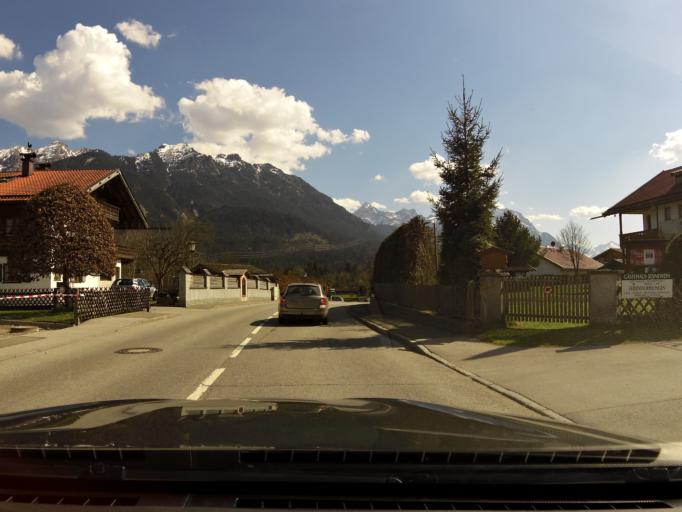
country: DE
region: Bavaria
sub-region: Upper Bavaria
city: Wallgau
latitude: 47.5183
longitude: 11.2834
